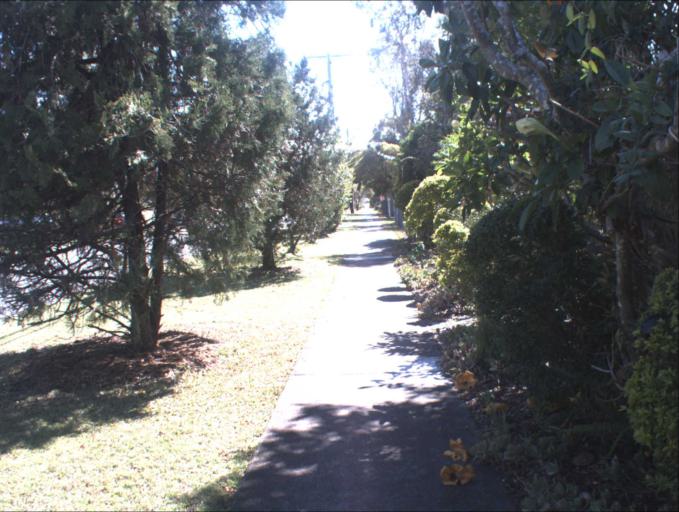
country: AU
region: Queensland
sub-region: Logan
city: Waterford West
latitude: -27.6802
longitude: 153.1064
